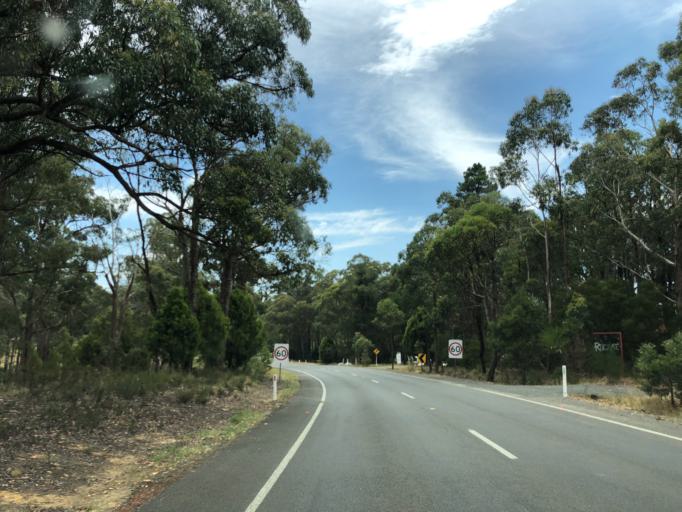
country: AU
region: Victoria
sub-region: Moorabool
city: Bacchus Marsh
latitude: -37.4829
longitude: 144.3042
